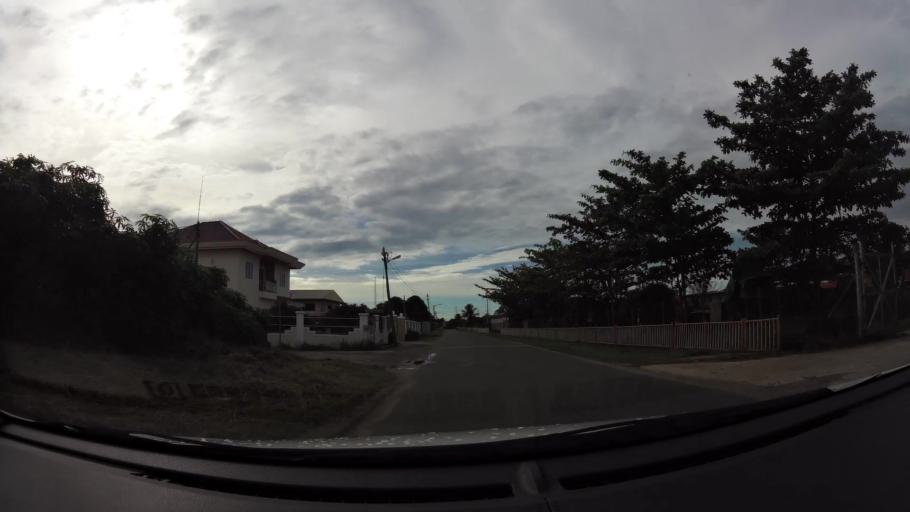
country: BN
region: Belait
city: Seria
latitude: 4.6136
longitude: 114.3552
